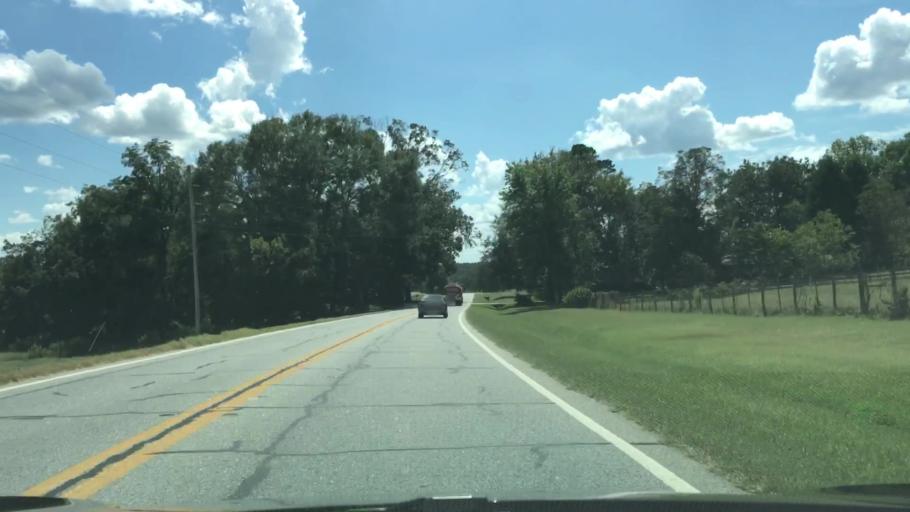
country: US
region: Georgia
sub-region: Oconee County
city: Watkinsville
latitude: 33.7467
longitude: -83.3013
